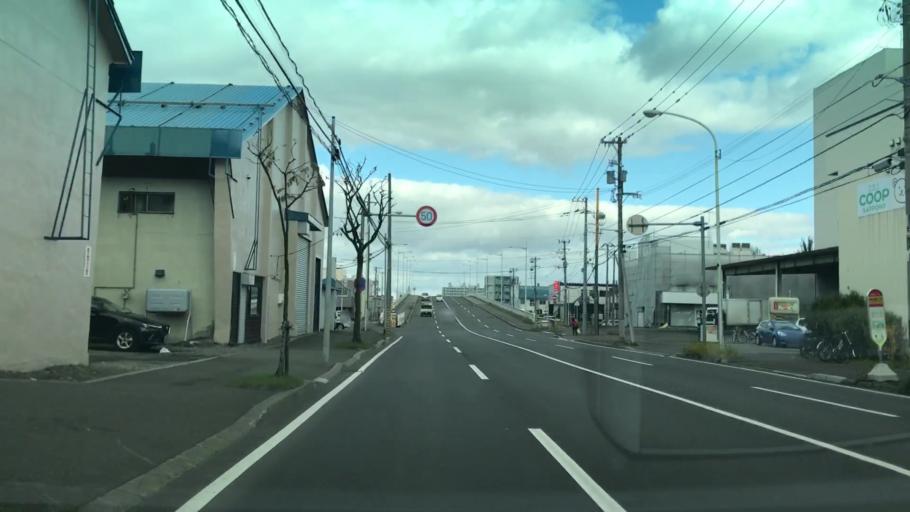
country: JP
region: Hokkaido
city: Sapporo
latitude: 43.0598
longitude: 141.4003
